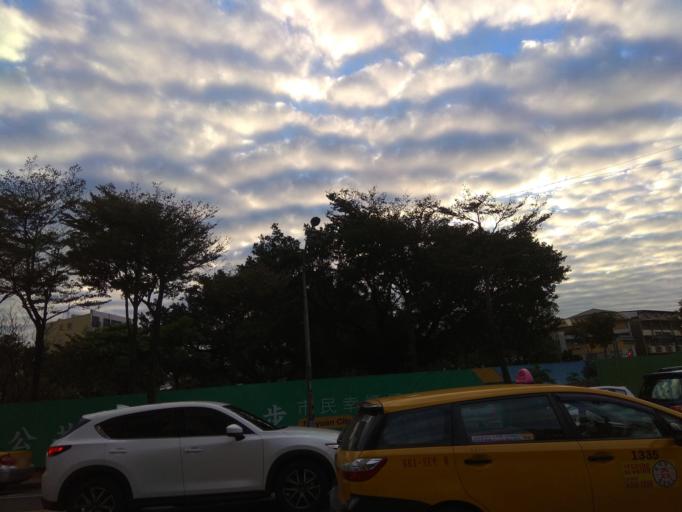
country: TW
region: Taiwan
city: Taoyuan City
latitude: 24.9964
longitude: 121.3068
